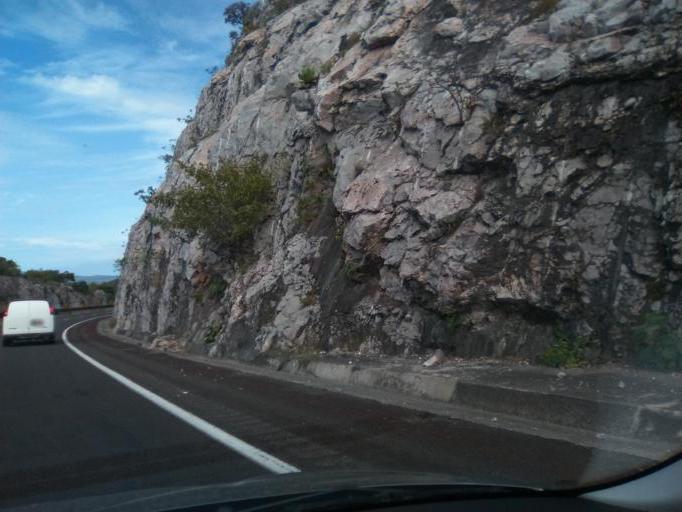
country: MX
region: Guerrero
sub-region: Eduardo Neri
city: Tlanipatla
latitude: 17.8635
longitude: -99.4058
